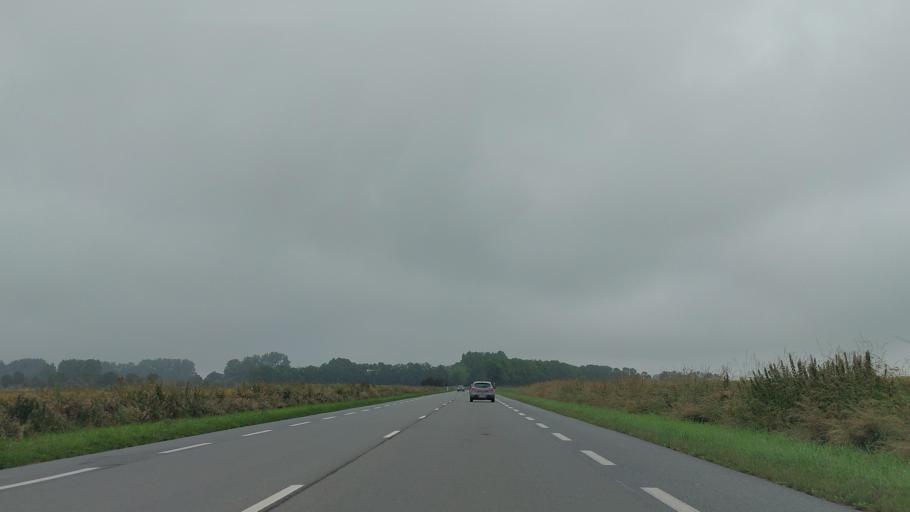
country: FR
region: Picardie
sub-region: Departement de la Somme
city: Woincourt
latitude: 50.0707
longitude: 1.5213
